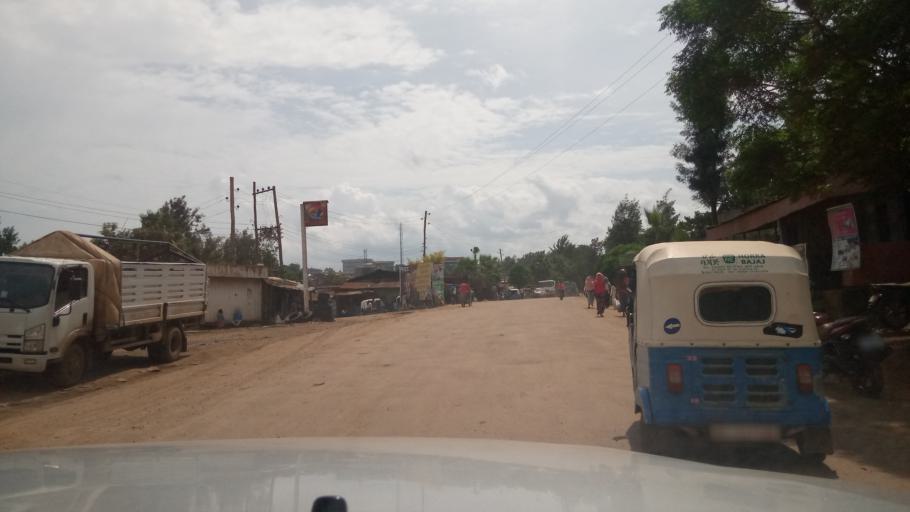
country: ET
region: Oromiya
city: Agaro
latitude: 7.8545
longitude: 36.5910
